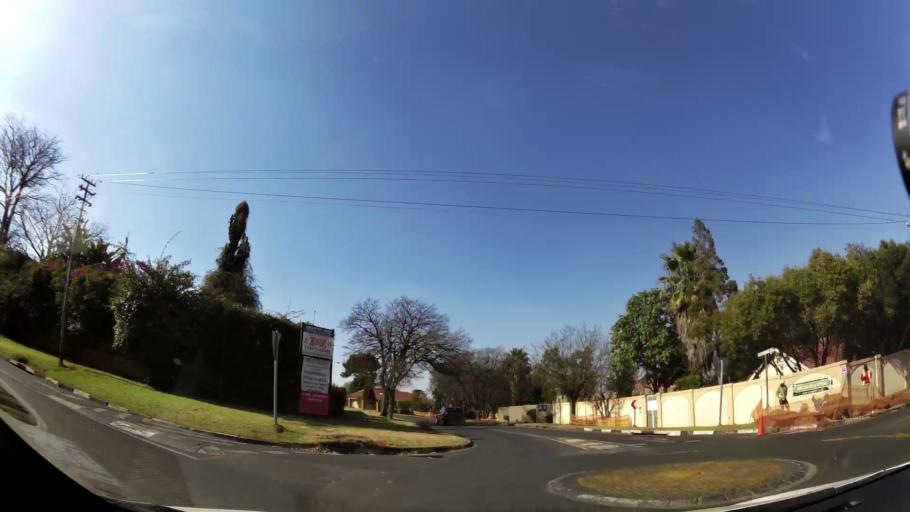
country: ZA
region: Gauteng
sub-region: City of Johannesburg Metropolitan Municipality
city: Johannesburg
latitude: -26.2642
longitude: 28.0644
